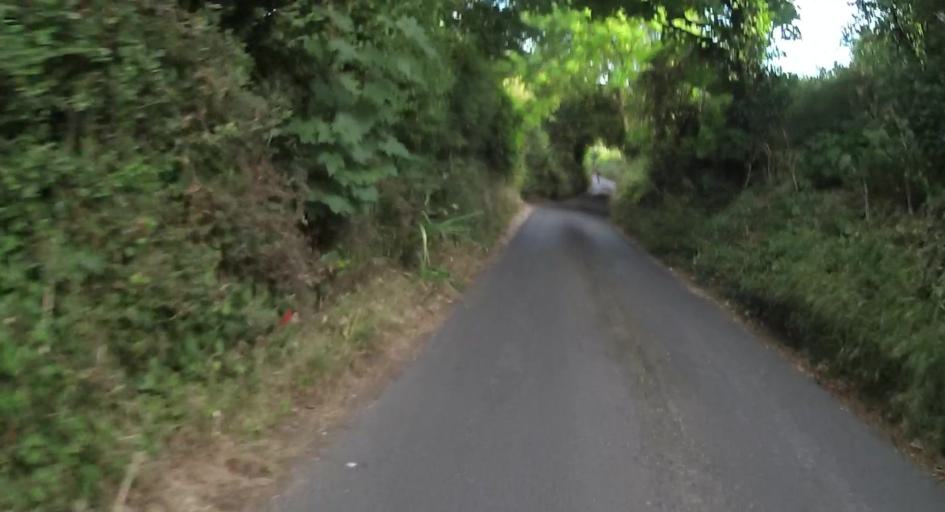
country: GB
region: England
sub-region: Dorset
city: Wareham
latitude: 50.6365
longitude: -2.0953
